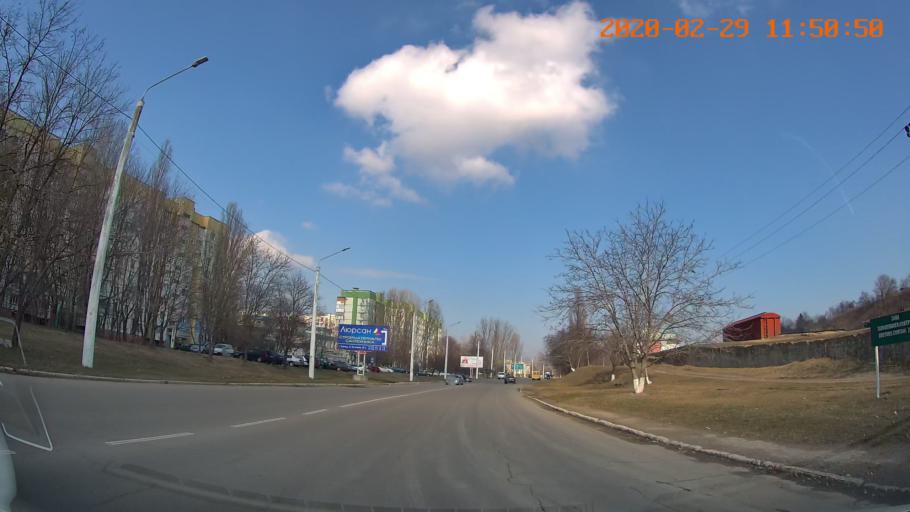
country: MD
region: Telenesti
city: Ribnita
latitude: 47.7613
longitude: 28.9897
